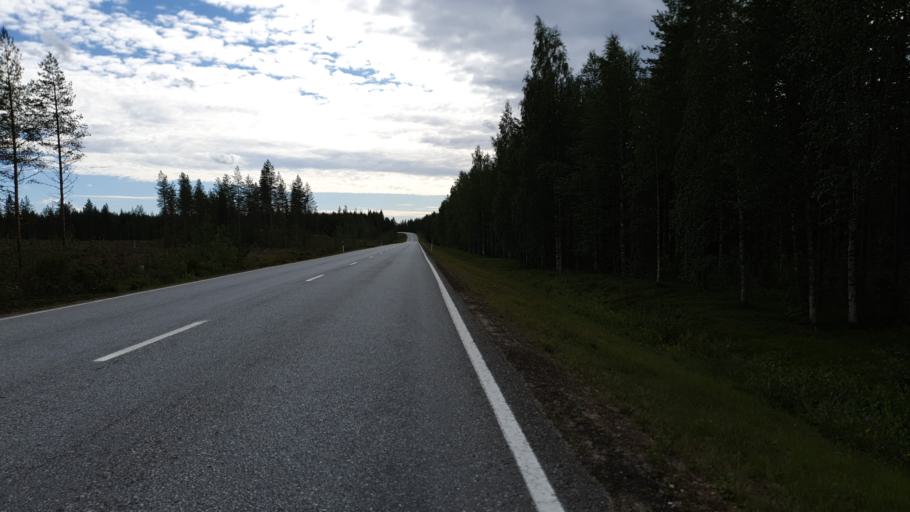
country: FI
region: Kainuu
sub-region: Kehys-Kainuu
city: Kuhmo
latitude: 64.4806
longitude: 29.7472
